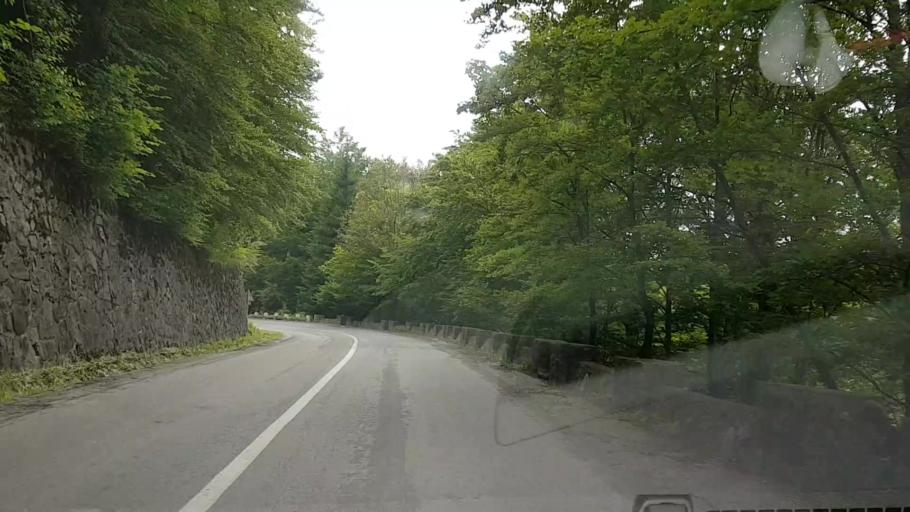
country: RO
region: Neamt
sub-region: Comuna Pangarati
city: Pangarati
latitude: 46.9882
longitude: 26.1185
